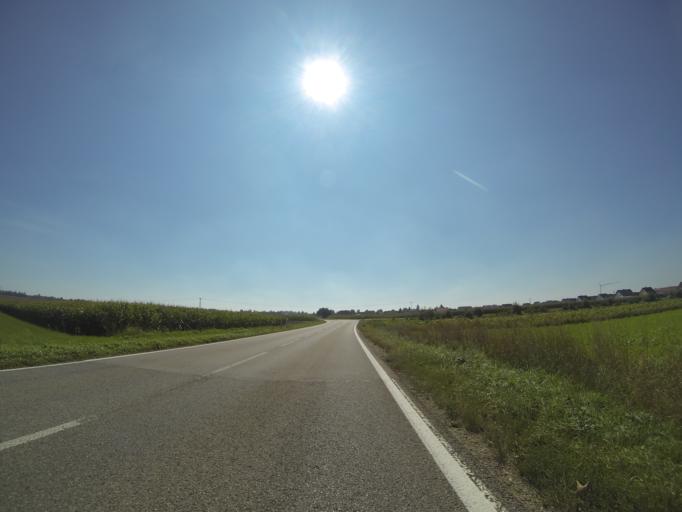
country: DE
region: Baden-Wuerttemberg
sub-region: Tuebingen Region
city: Achstetten
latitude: 48.2860
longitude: 9.9048
